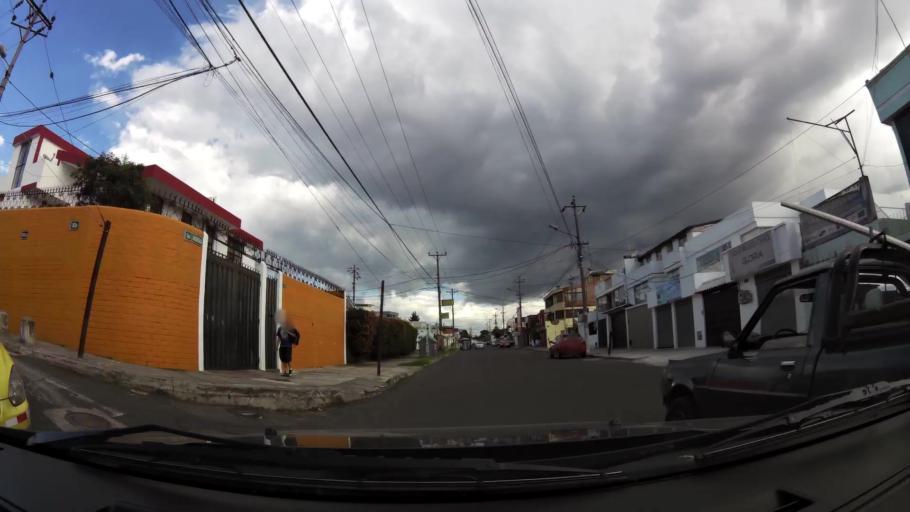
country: EC
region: Pichincha
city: Quito
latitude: -0.1185
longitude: -78.4888
